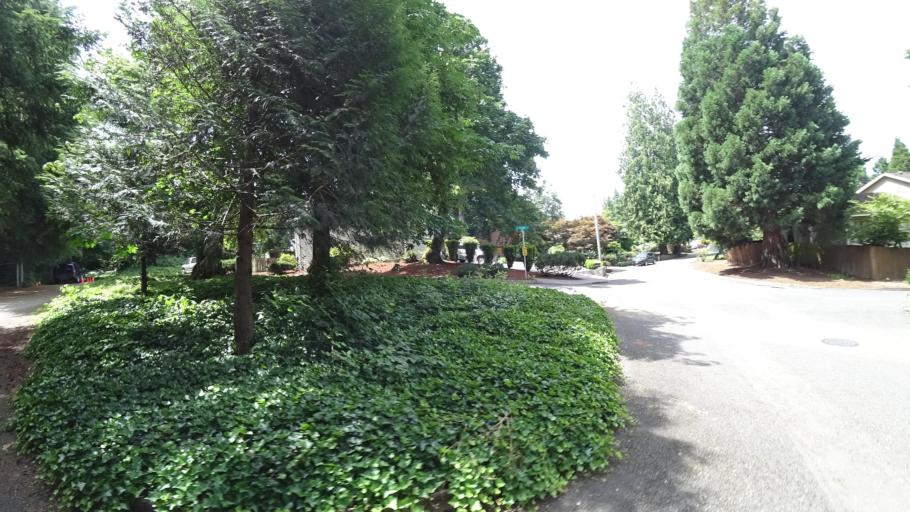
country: US
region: Oregon
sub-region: Multnomah County
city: Fairview
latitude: 45.5443
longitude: -122.4926
